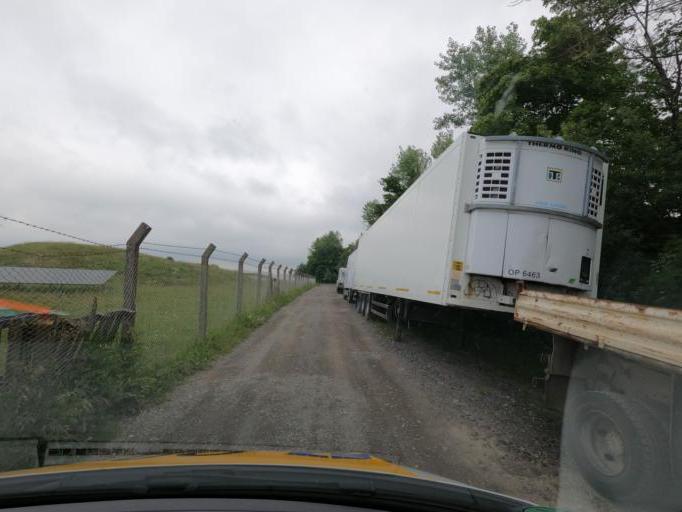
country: DE
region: Thuringia
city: Kreuzebra
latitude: 51.3338
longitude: 10.2577
